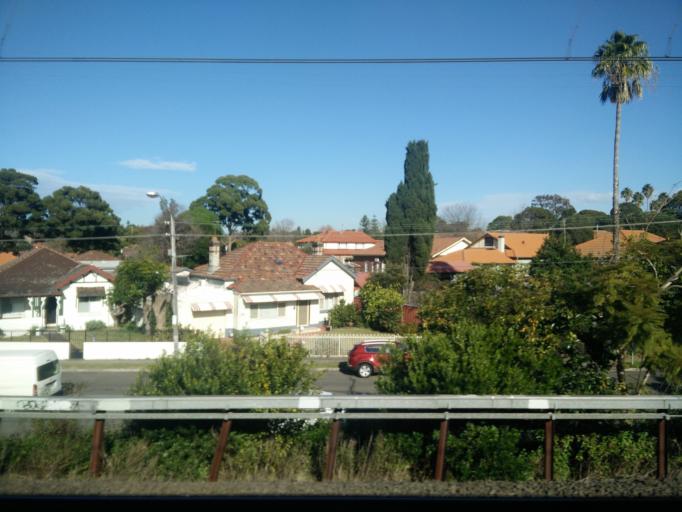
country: AU
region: New South Wales
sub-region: Ashfield
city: Croydon
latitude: -33.8807
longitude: 151.1118
